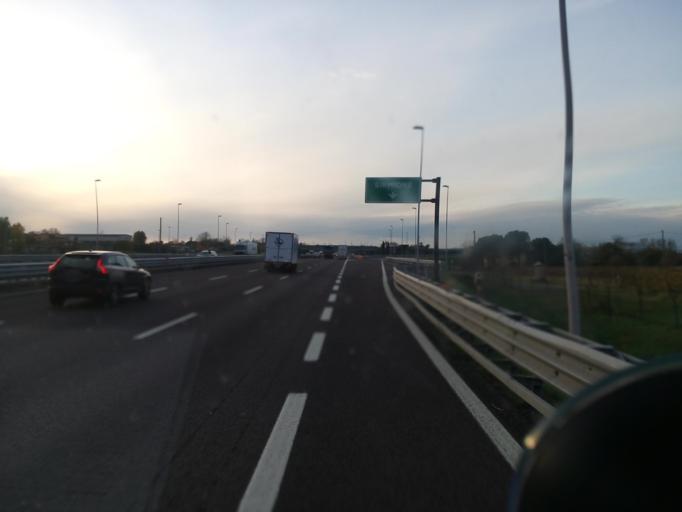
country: IT
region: Lombardy
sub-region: Provincia di Brescia
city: San Martino della Battaglia
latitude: 45.4337
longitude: 10.6160
